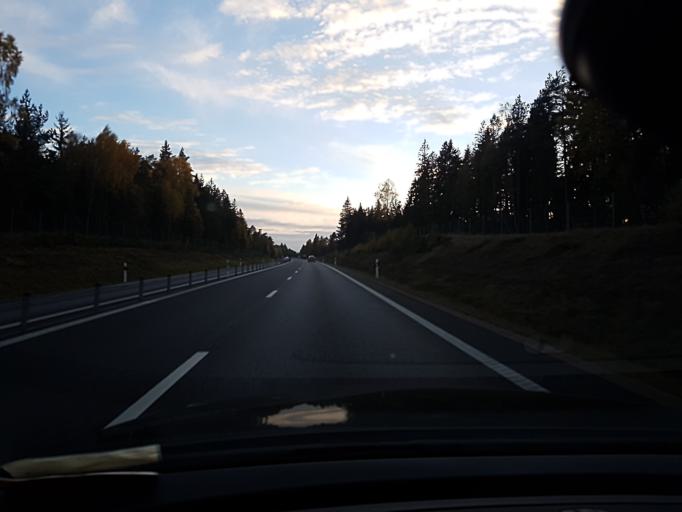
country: SE
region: Kronoberg
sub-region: Ljungby Kommun
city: Ljungby
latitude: 56.7822
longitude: 13.8216
